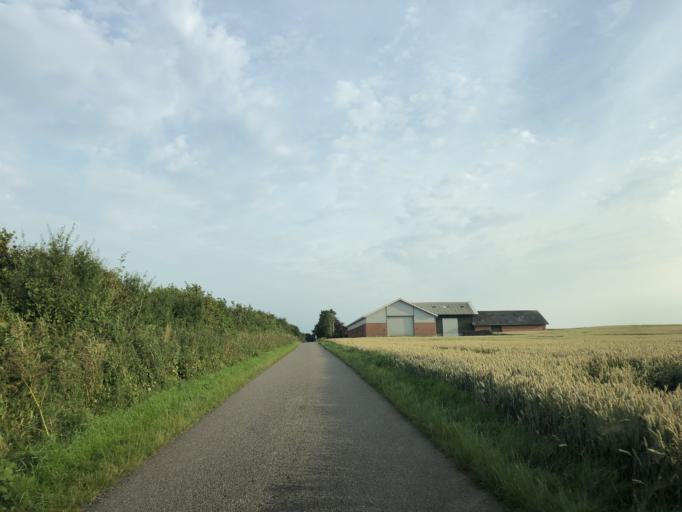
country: DK
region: South Denmark
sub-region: Vejle Kommune
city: Borkop
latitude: 55.5924
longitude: 9.6344
